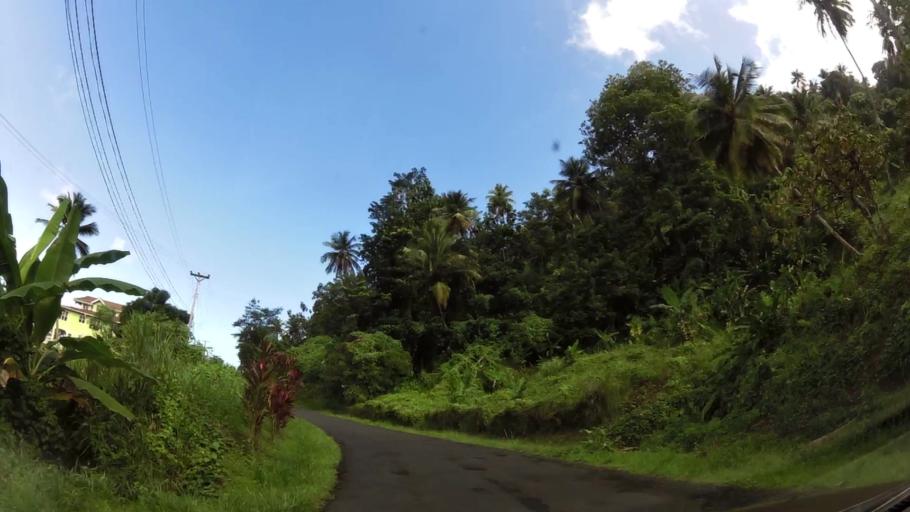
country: DM
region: Saint Andrew
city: Marigot
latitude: 15.5157
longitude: -61.2684
